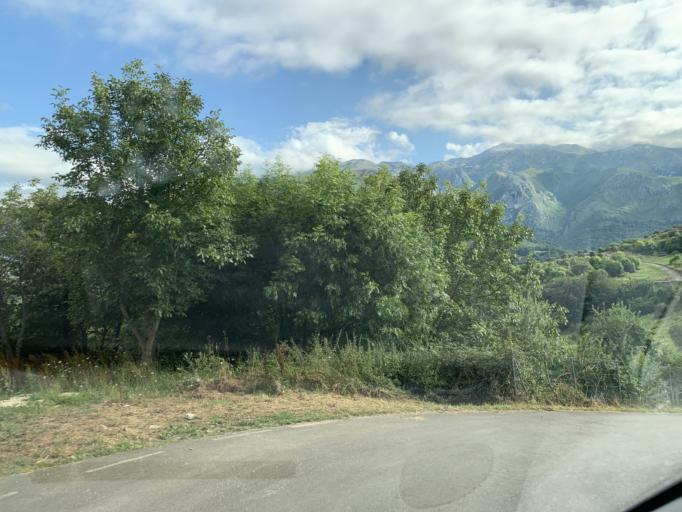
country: ES
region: Asturias
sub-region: Province of Asturias
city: Carrena
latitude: 43.3262
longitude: -4.8595
